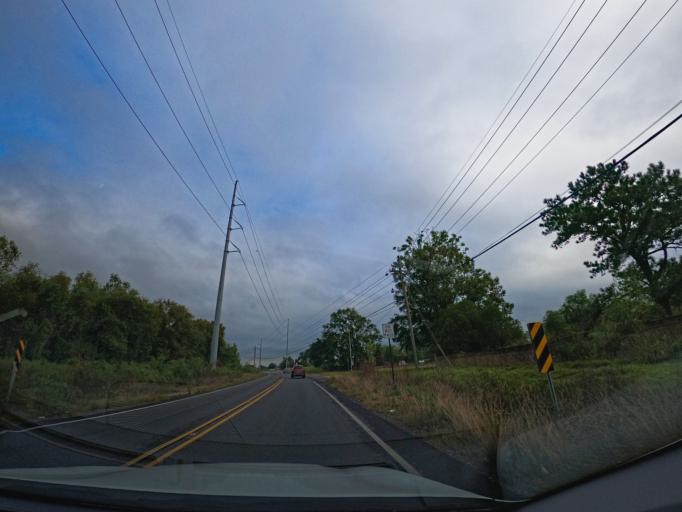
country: US
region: Louisiana
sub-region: Terrebonne Parish
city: Presquille
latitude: 29.5297
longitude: -90.6746
